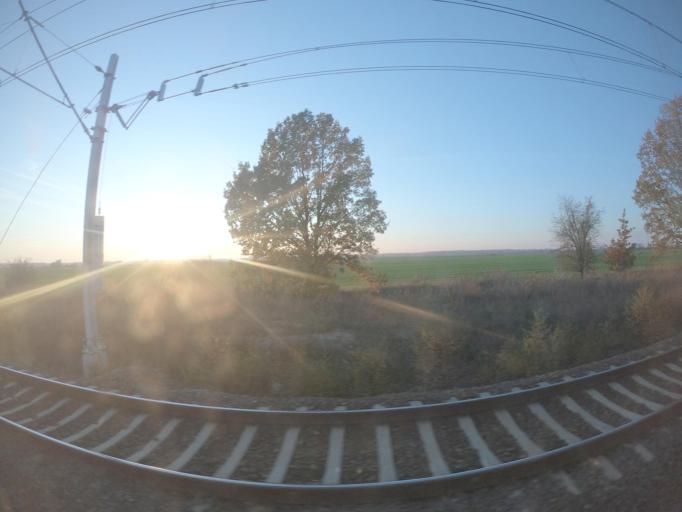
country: PL
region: Lubusz
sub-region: Powiat slubicki
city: Gorzyca
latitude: 52.5246
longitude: 14.6505
